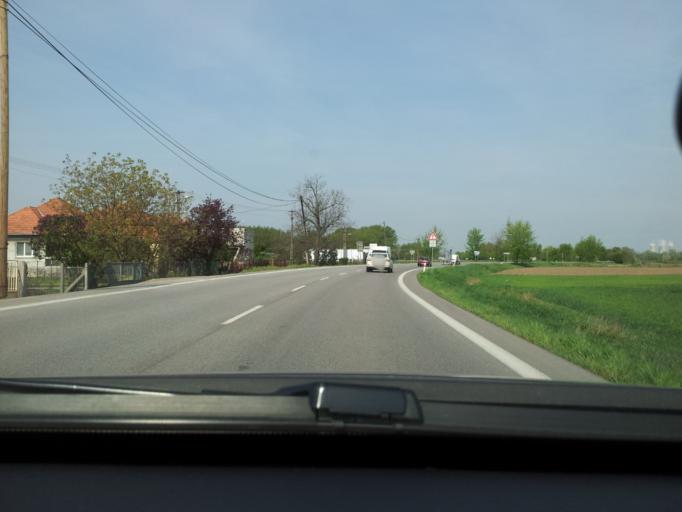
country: SK
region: Nitriansky
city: Levice
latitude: 48.1970
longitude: 18.5394
